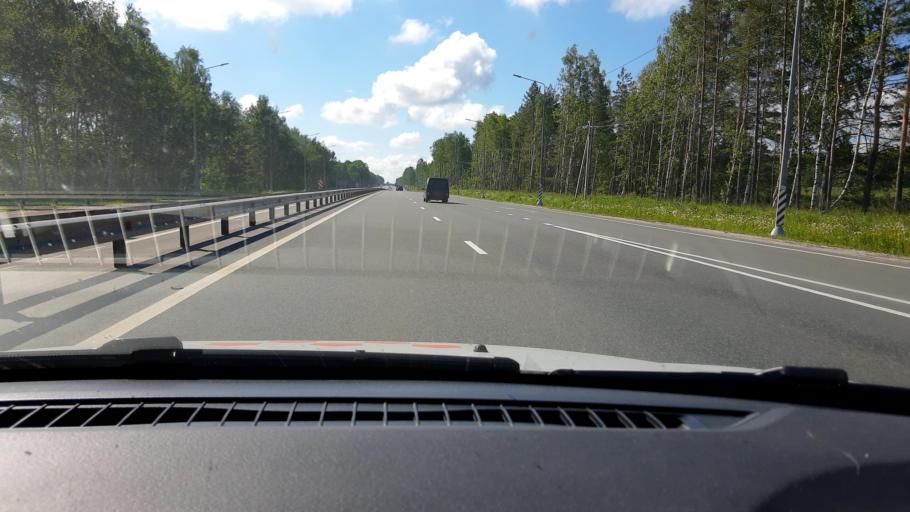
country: RU
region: Nizjnij Novgorod
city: Burevestnik
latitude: 56.0637
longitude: 43.9416
